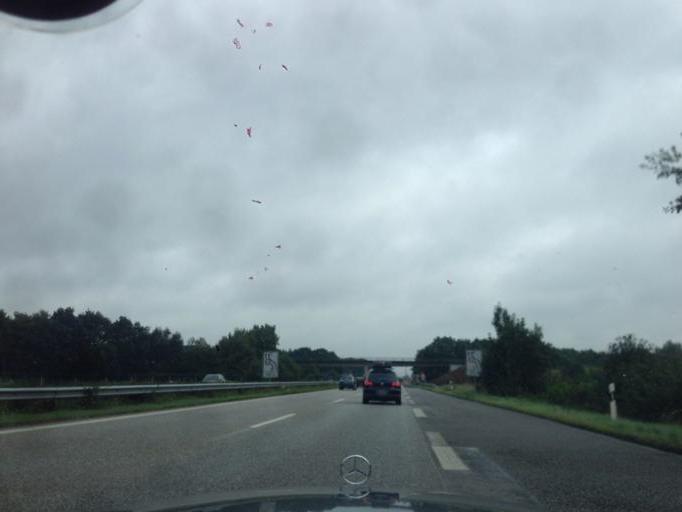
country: DE
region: Schleswig-Holstein
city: Bimohlen
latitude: 53.9263
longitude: 9.9409
